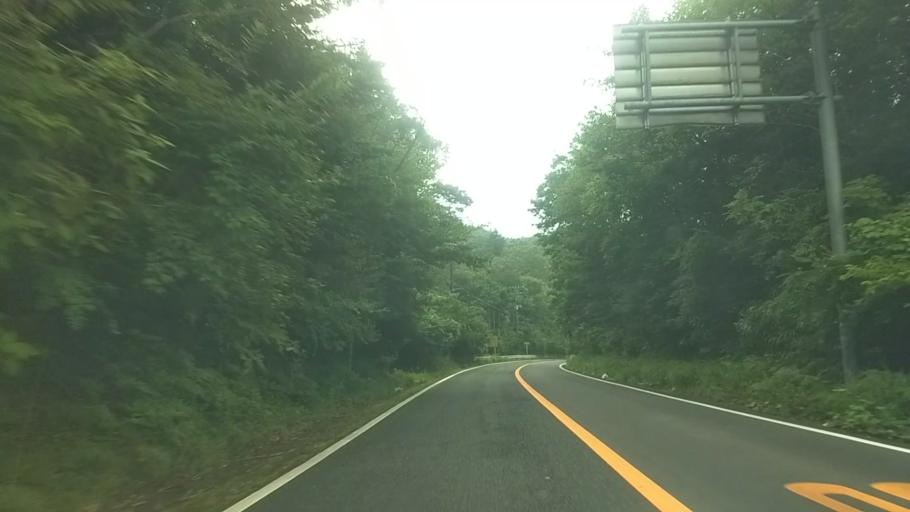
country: JP
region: Chiba
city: Kawaguchi
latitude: 35.2049
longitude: 140.0684
